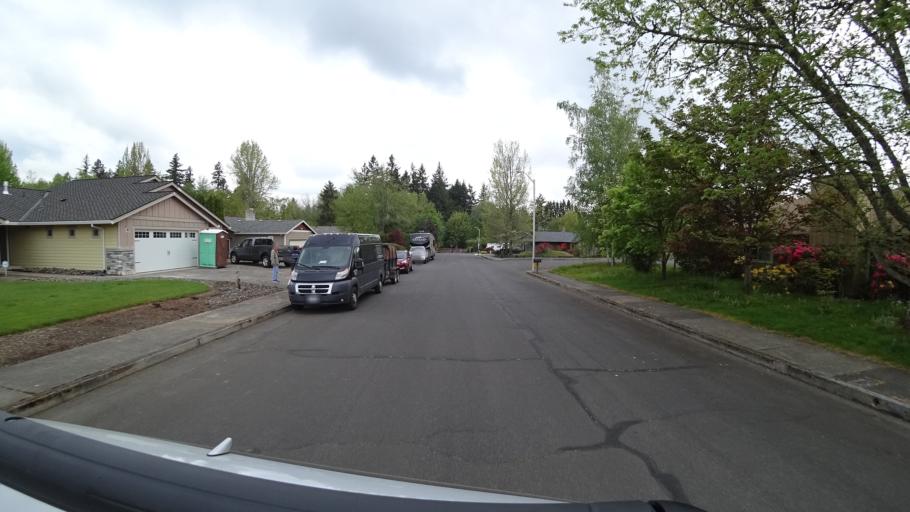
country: US
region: Oregon
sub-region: Washington County
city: Hillsboro
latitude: 45.5320
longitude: -122.9819
